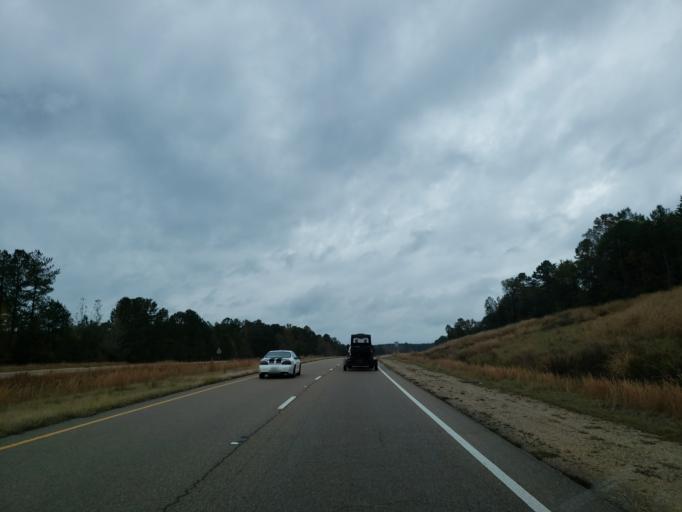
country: US
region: Mississippi
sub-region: Wayne County
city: Waynesboro
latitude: 31.7258
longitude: -88.6440
